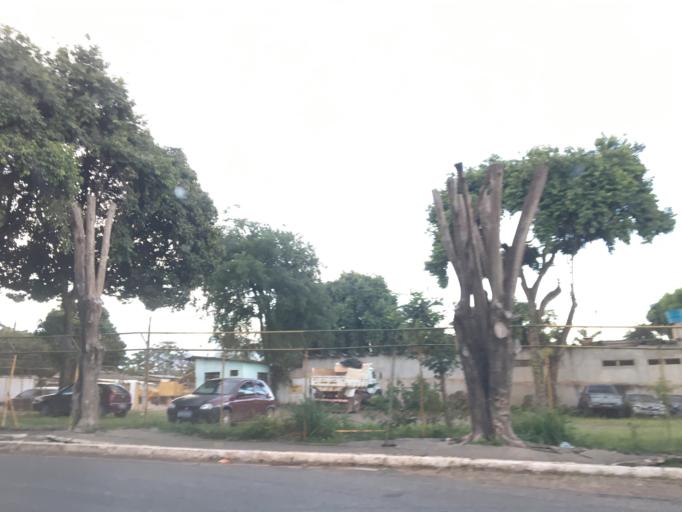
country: BR
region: Federal District
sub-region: Brasilia
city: Brasilia
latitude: -15.8245
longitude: -47.9719
